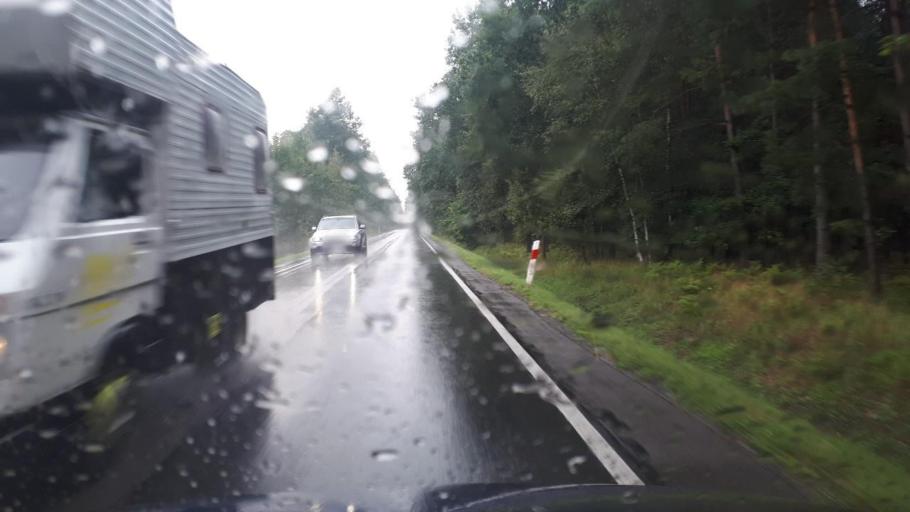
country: PL
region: Silesian Voivodeship
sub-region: Powiat tarnogorski
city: Tworog
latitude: 50.5301
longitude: 18.6864
